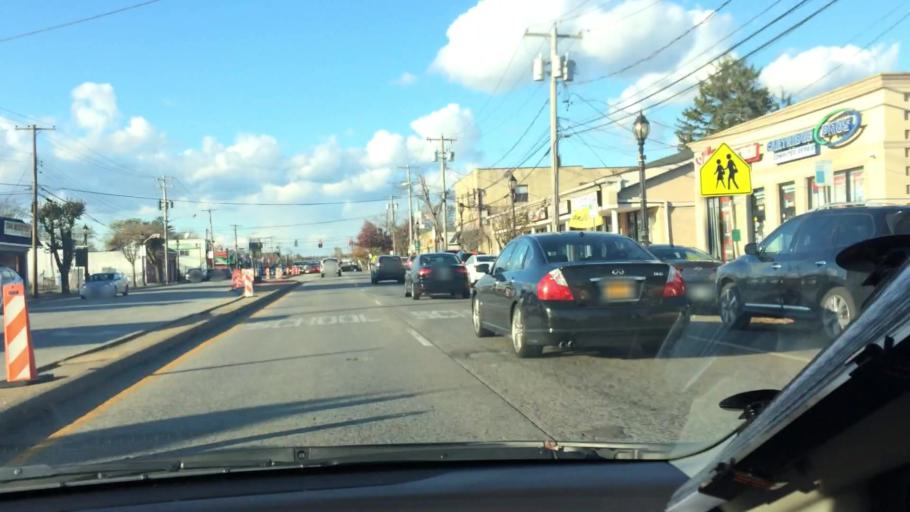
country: US
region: New York
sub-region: Suffolk County
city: Deer Park
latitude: 40.7576
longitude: -73.3275
